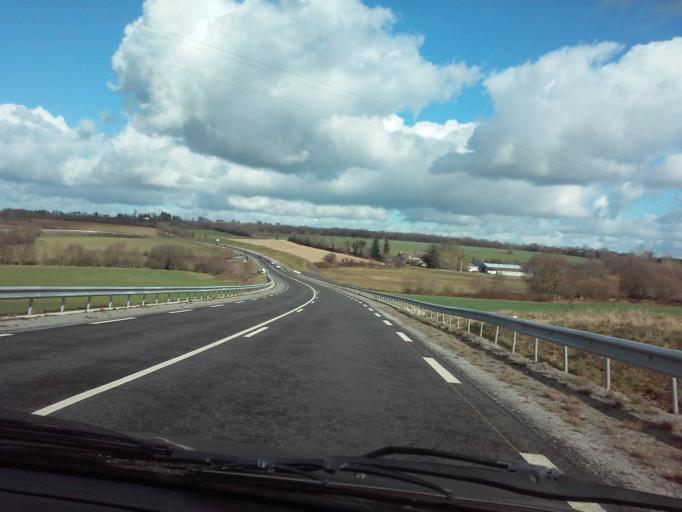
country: FR
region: Brittany
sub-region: Departement d'Ille-et-Vilaine
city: Poce-les-Bois
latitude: 48.0899
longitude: -1.2321
